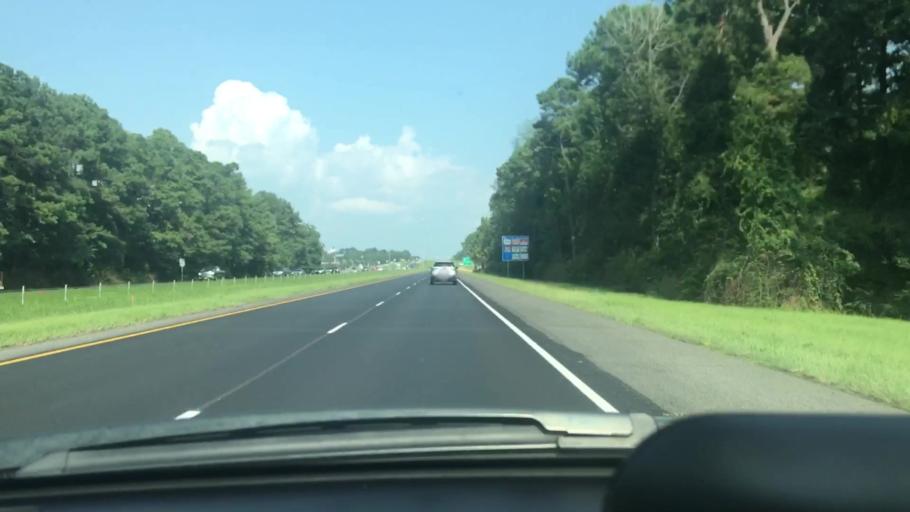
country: US
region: Louisiana
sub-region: Tangipahoa Parish
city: Hammond
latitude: 30.4789
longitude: -90.4672
